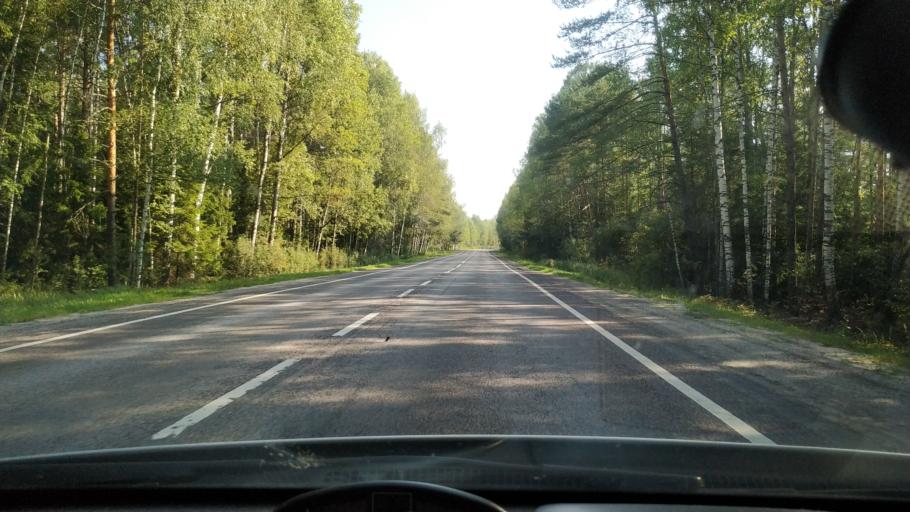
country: RU
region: Moskovskaya
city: Dmitrovskiy Pogost
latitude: 55.2307
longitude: 39.9454
